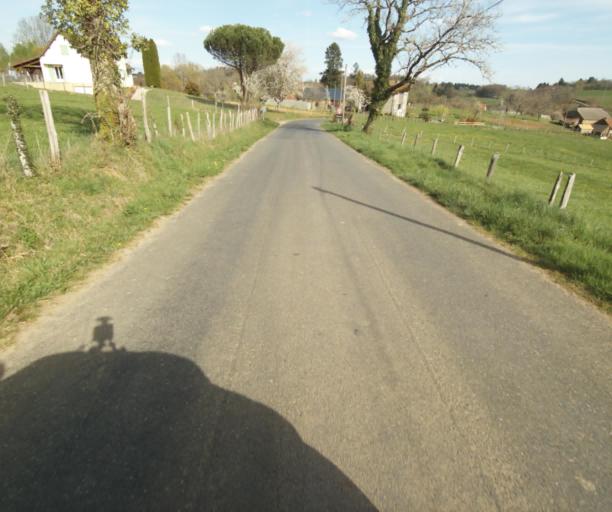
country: FR
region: Limousin
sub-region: Departement de la Correze
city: Seilhac
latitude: 45.3306
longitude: 1.7315
